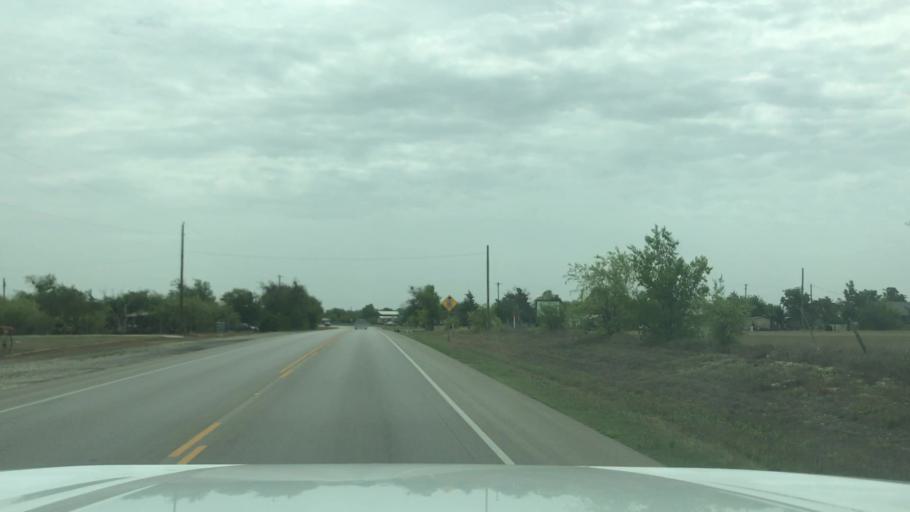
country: US
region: Texas
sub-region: Erath County
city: Dublin
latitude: 32.0902
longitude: -98.3605
